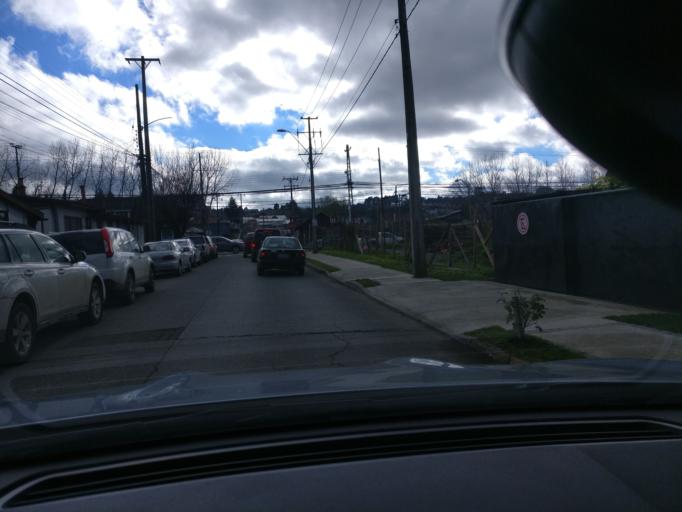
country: CL
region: Los Lagos
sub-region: Provincia de Llanquihue
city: Puerto Varas
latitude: -41.3180
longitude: -72.9899
